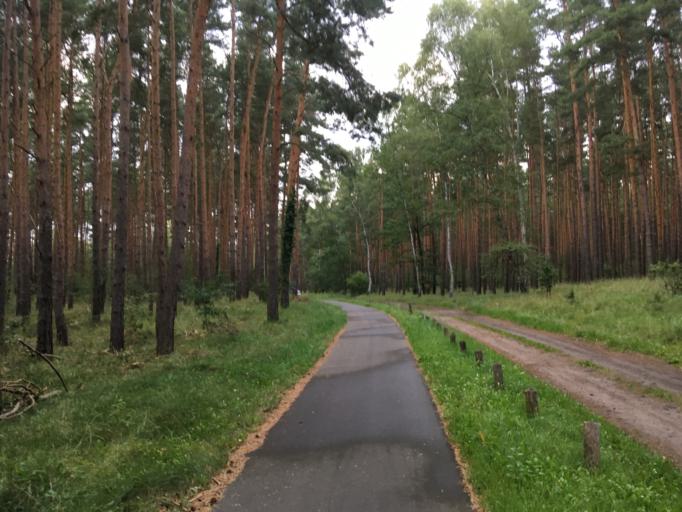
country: DE
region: Brandenburg
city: Erkner
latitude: 52.3901
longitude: 13.7768
